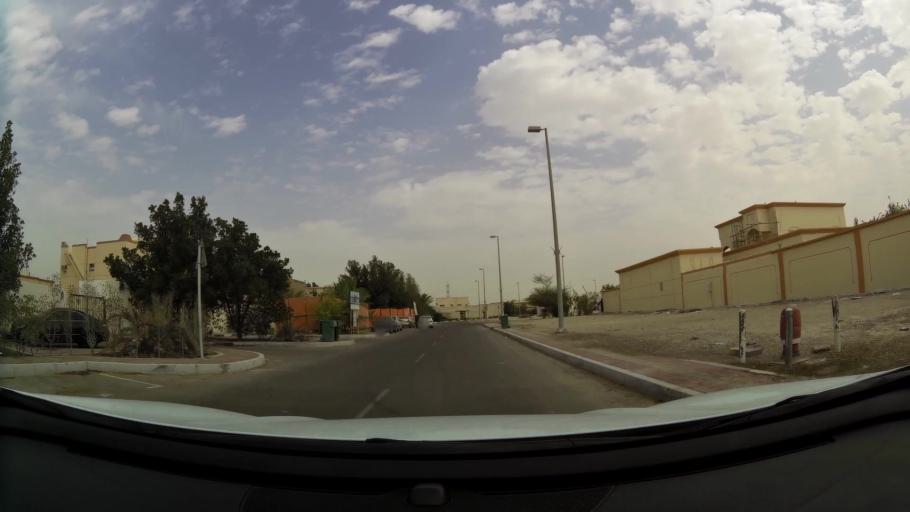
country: AE
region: Abu Dhabi
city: Abu Dhabi
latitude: 24.3109
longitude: 54.6336
